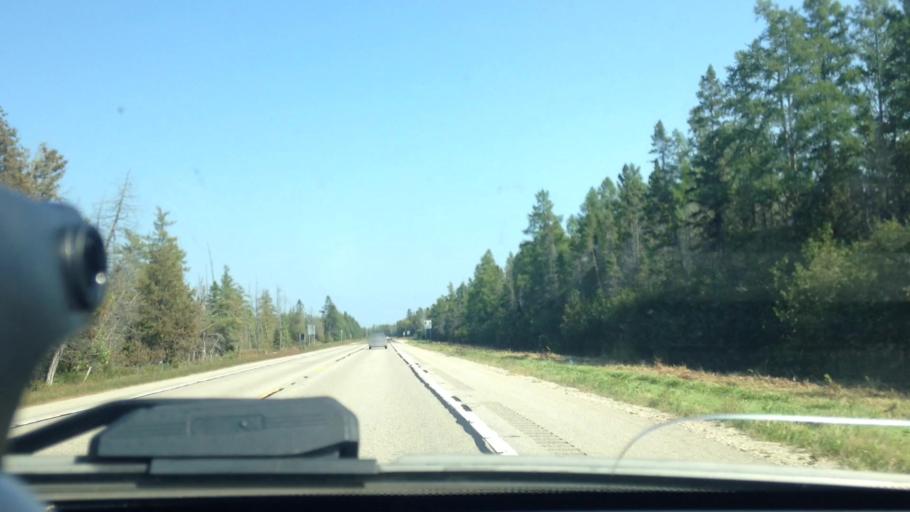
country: US
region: Michigan
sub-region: Luce County
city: Newberry
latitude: 46.3036
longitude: -85.2431
